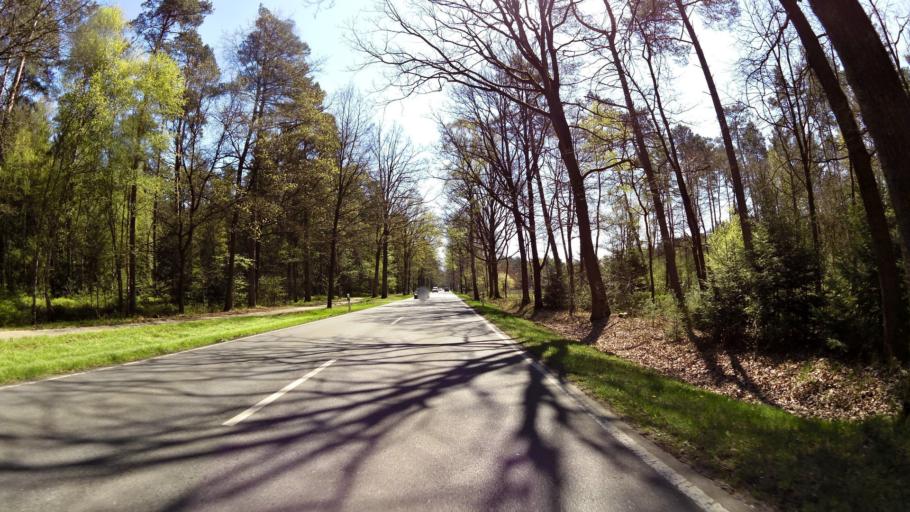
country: DE
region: Lower Saxony
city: Neuenkirchen
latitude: 53.0178
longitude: 9.7755
